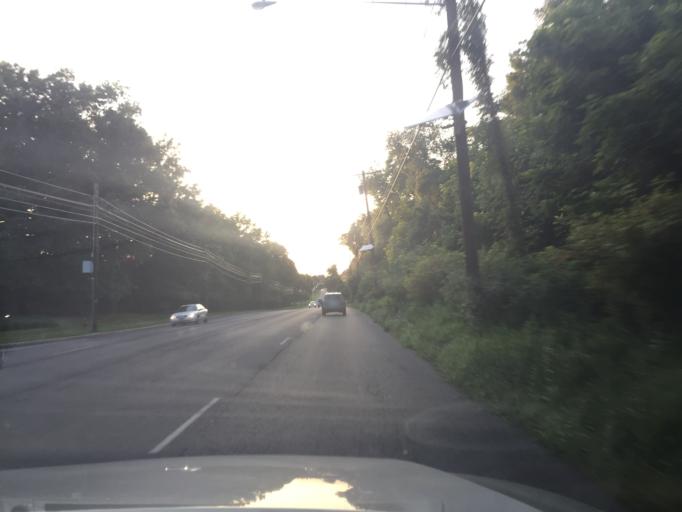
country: US
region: New Jersey
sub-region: Mercer County
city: Princeton Junction
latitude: 40.2971
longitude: -74.5999
